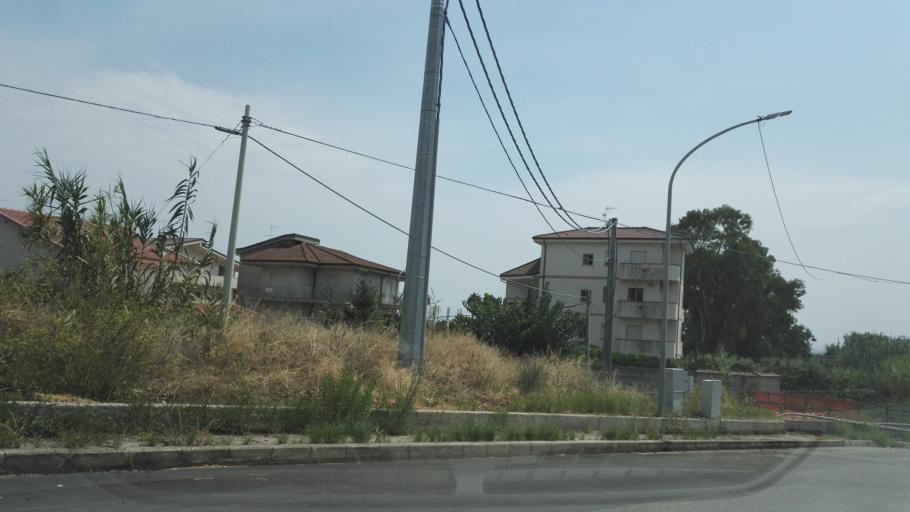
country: IT
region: Calabria
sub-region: Provincia di Reggio Calabria
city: Riace Marina
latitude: 38.3874
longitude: 16.5235
